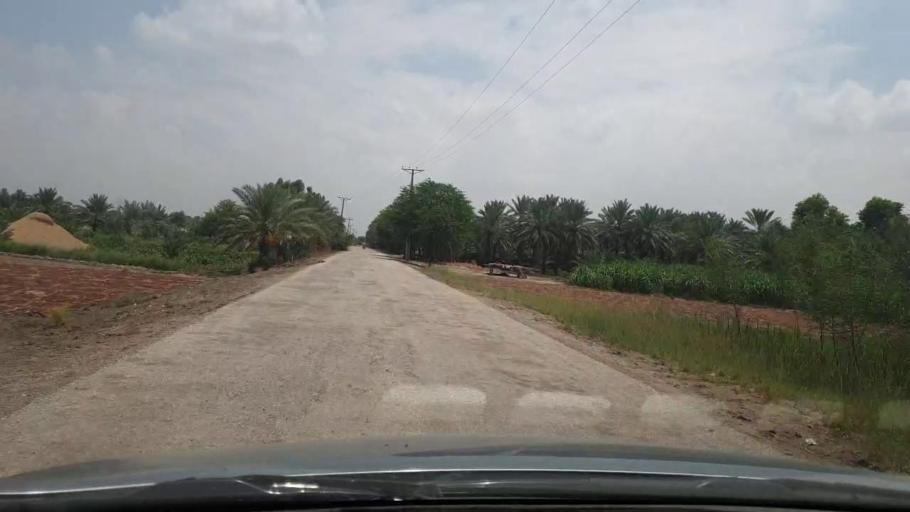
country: PK
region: Sindh
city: Khairpur
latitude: 27.4374
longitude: 68.7550
